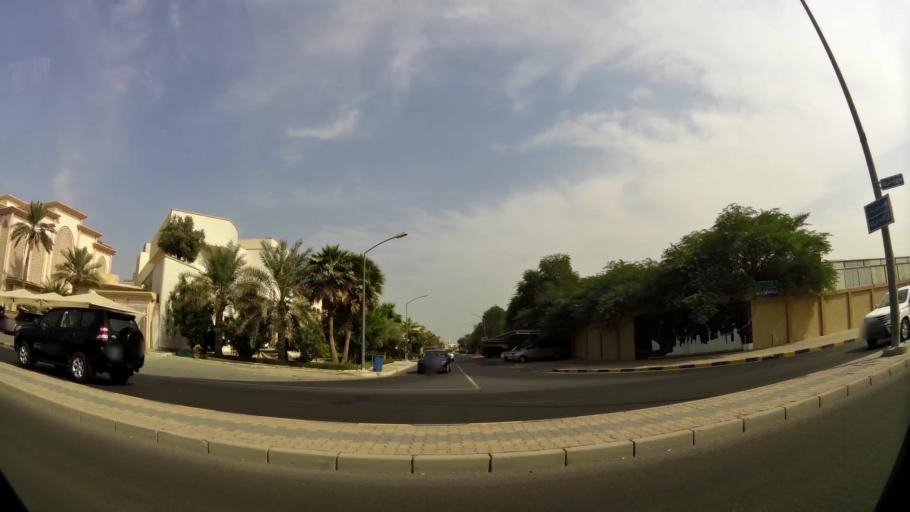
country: KW
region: Al Asimah
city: Ash Shamiyah
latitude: 29.3542
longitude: 47.9684
